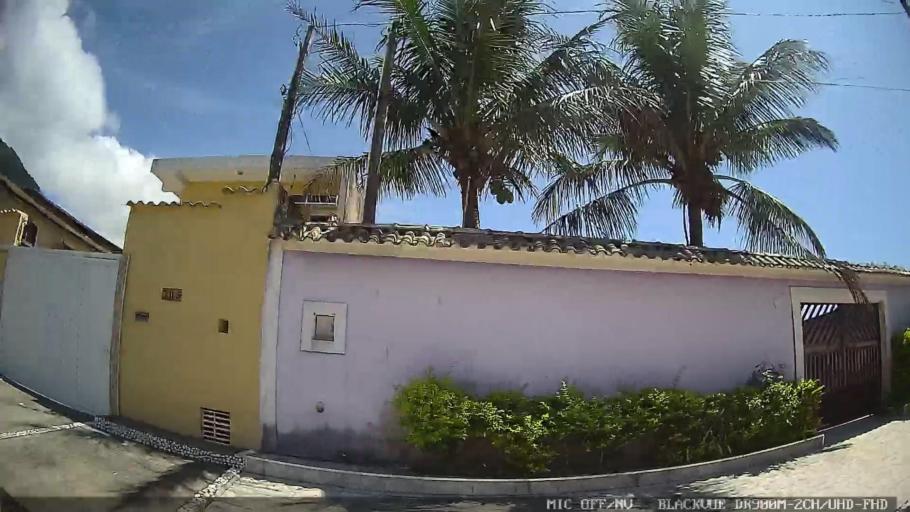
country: BR
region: Sao Paulo
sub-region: Peruibe
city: Peruibe
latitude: -24.3321
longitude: -47.0048
